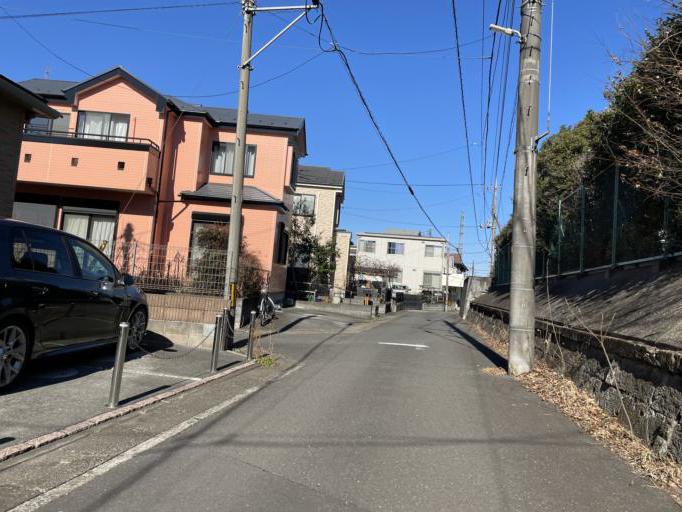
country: JP
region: Saitama
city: Oi
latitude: 35.8167
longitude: 139.5421
